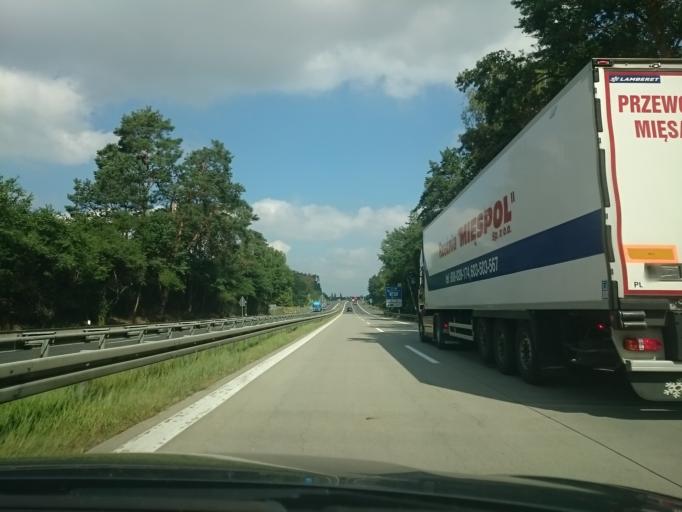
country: DE
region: Brandenburg
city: Melchow
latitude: 52.8763
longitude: 13.6945
